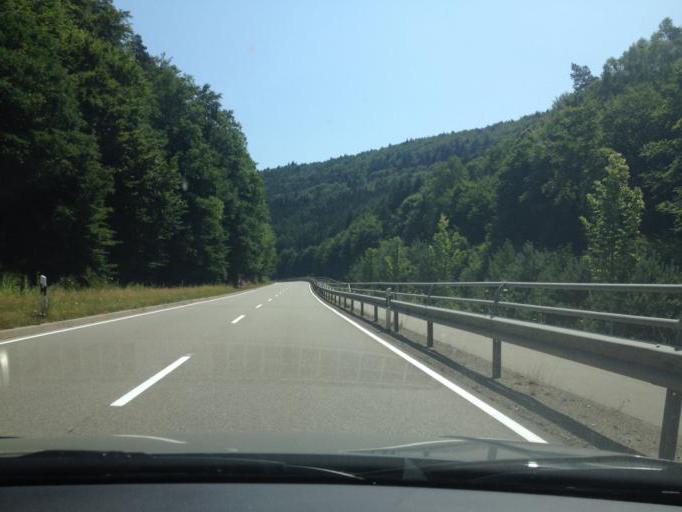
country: DE
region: Rheinland-Pfalz
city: Fischbach
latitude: 49.4385
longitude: 7.9490
